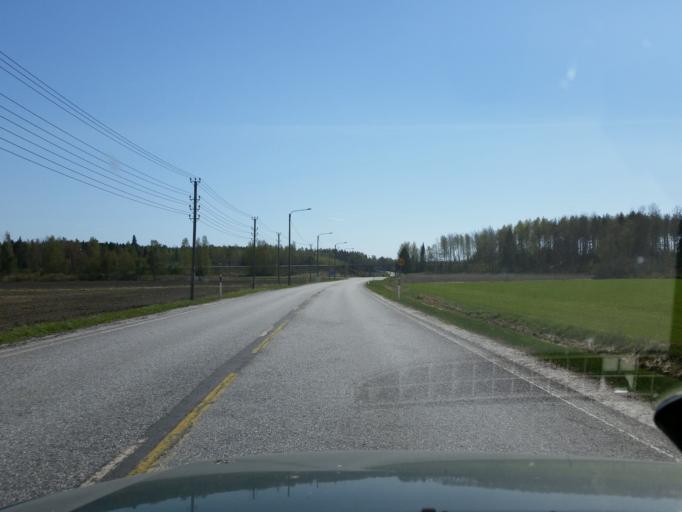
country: FI
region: Uusimaa
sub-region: Raaseporin
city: Inga
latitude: 60.0544
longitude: 23.9488
